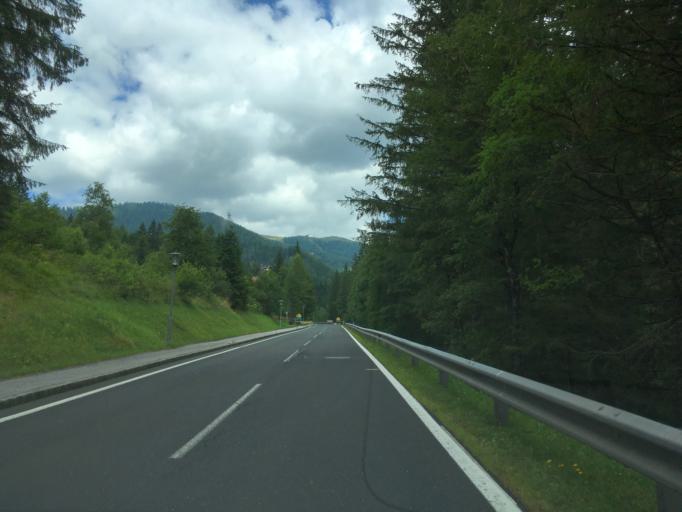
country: AT
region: Carinthia
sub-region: Politischer Bezirk Spittal an der Drau
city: Kleinkirchheim
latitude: 46.8296
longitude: 13.7690
